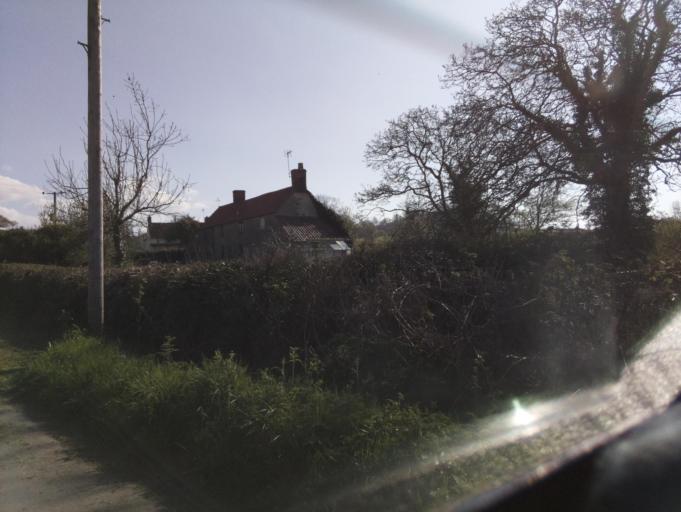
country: GB
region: England
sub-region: South Gloucestershire
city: Thornbury
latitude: 51.6159
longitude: -2.5552
